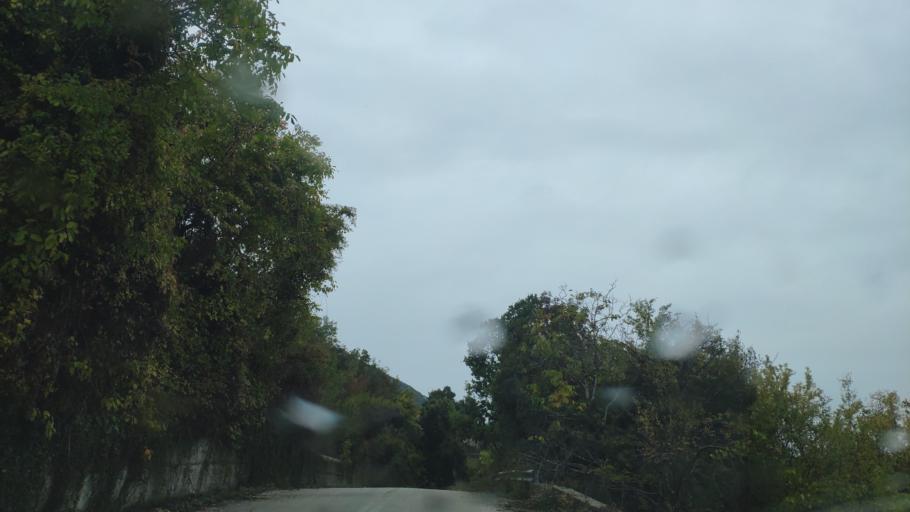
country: GR
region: Epirus
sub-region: Nomos Thesprotias
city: Paramythia
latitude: 39.4588
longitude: 20.6713
